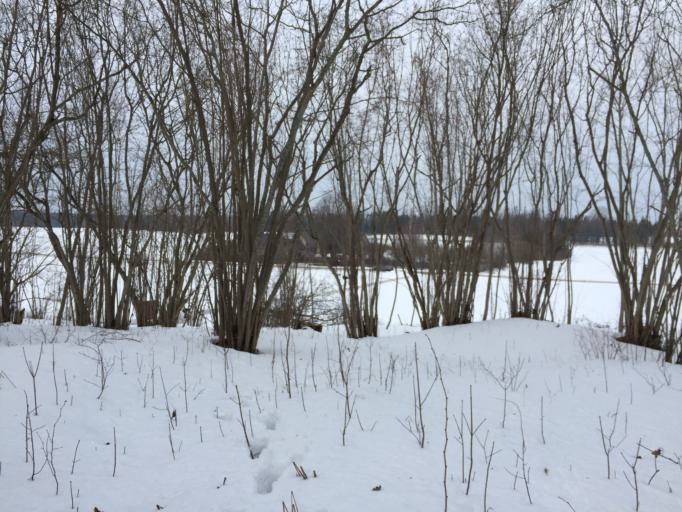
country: LV
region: Ikskile
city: Ikskile
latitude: 56.8440
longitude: 24.4535
